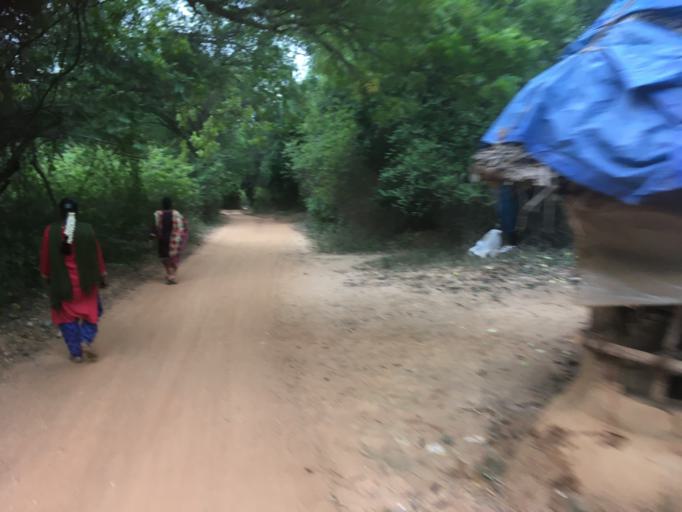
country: IN
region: Tamil Nadu
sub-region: Villupuram
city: Auroville
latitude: 12.0138
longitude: 79.8051
